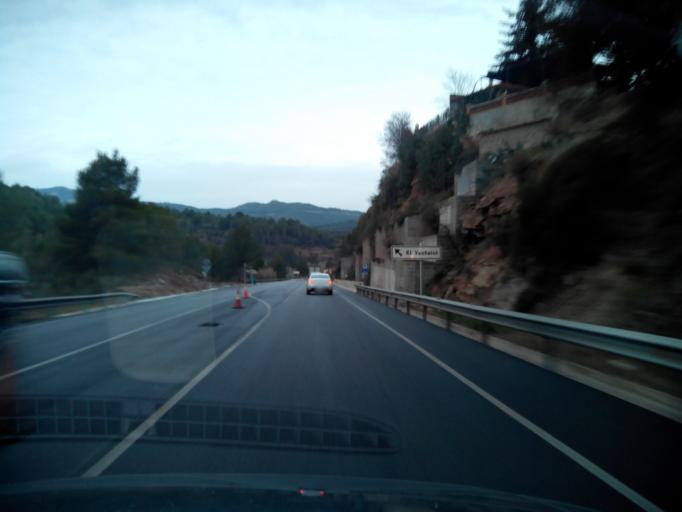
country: ES
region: Catalonia
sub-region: Provincia de Barcelona
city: Monistrol de Montserrat
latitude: 41.6154
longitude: 1.8703
